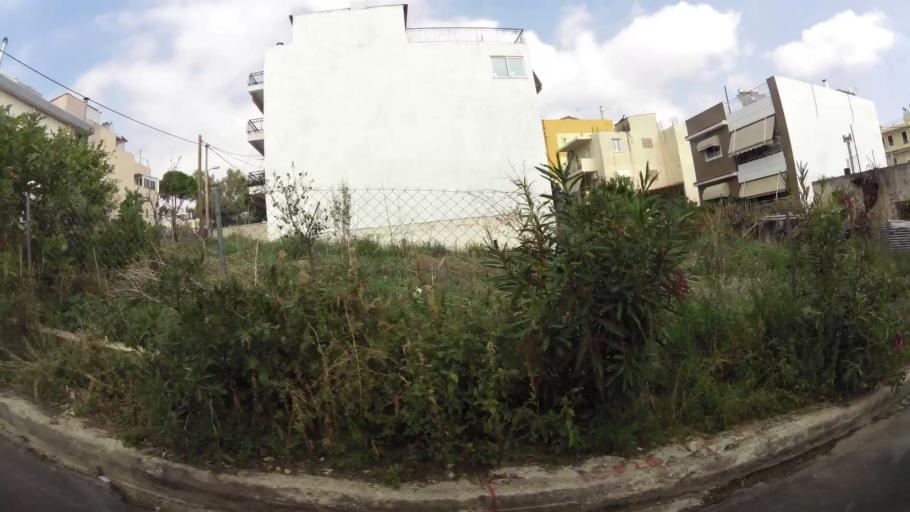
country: GR
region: Attica
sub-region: Nomarchia Dytikis Attikis
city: Zefyri
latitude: 38.0562
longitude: 23.7235
